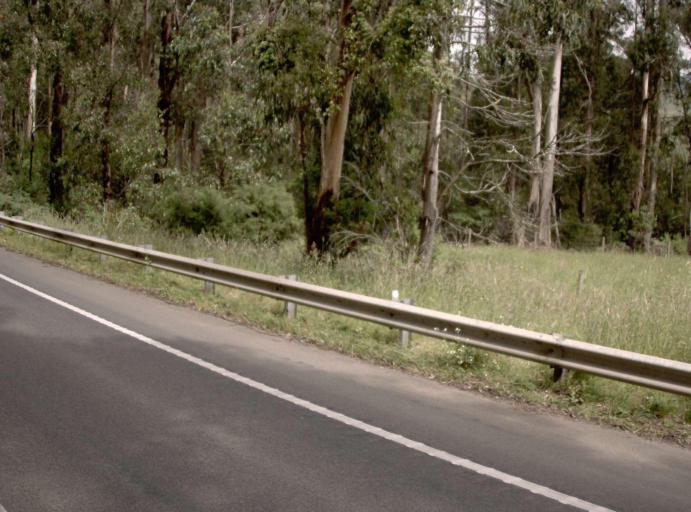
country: AU
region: Victoria
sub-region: Latrobe
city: Moe
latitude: -38.3596
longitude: 146.1866
